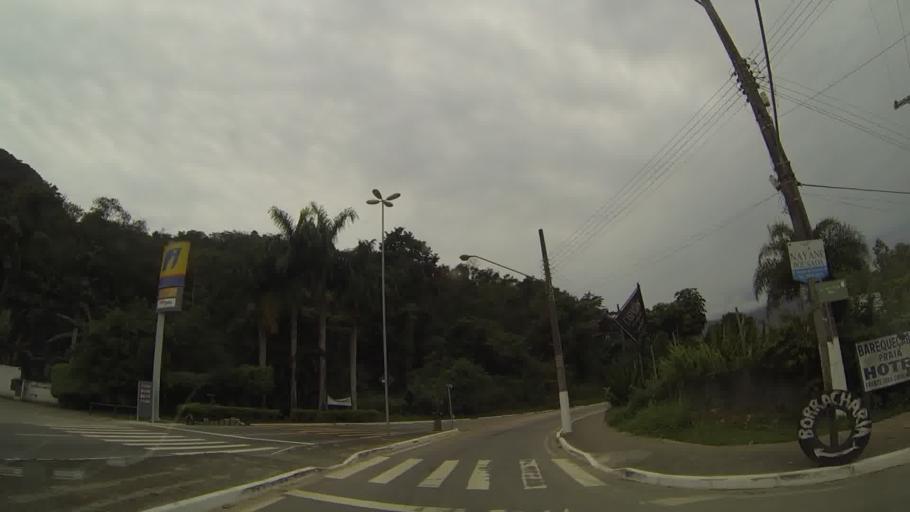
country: BR
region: Sao Paulo
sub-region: Sao Sebastiao
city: Sao Sebastiao
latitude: -23.8234
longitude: -45.4326
